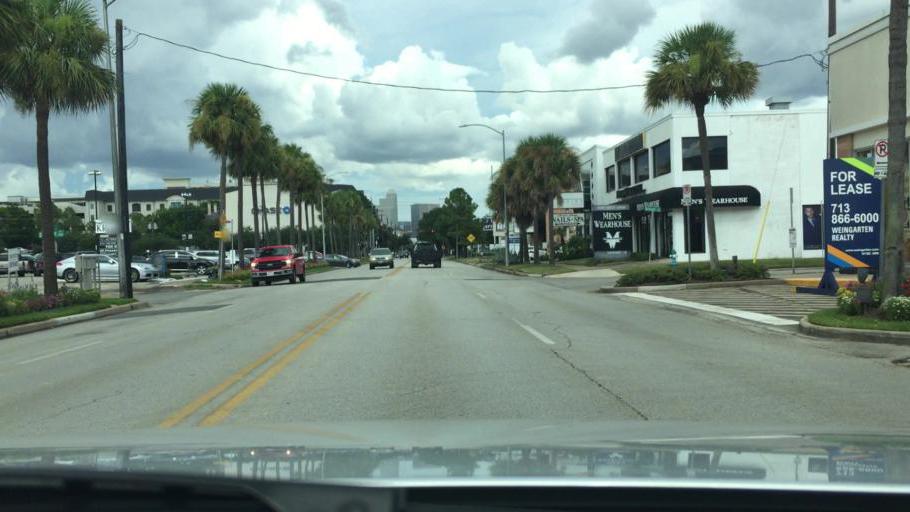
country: US
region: Texas
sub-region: Harris County
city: West University Place
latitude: 29.7531
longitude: -95.4068
